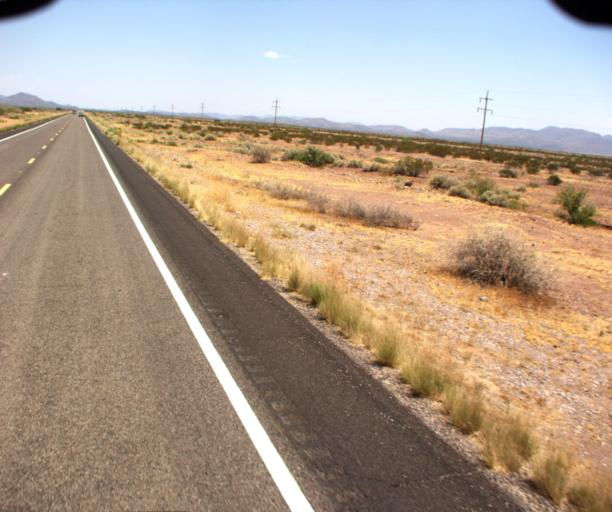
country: US
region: Arizona
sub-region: Graham County
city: Safford
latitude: 32.7761
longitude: -109.5070
